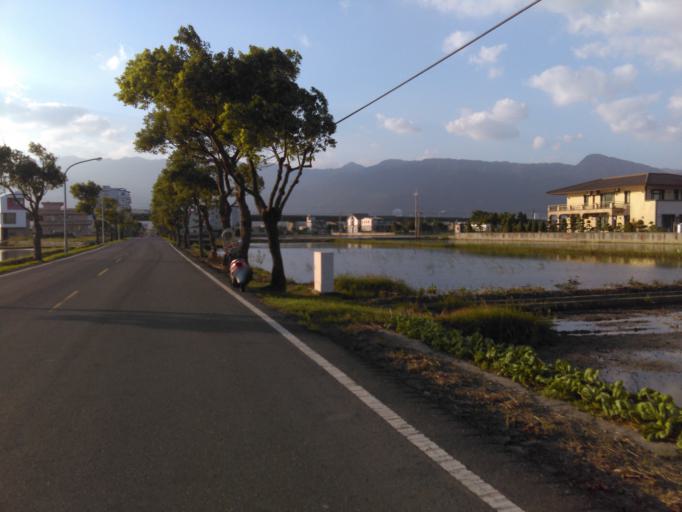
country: TW
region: Taiwan
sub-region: Yilan
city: Yilan
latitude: 24.7991
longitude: 121.7856
